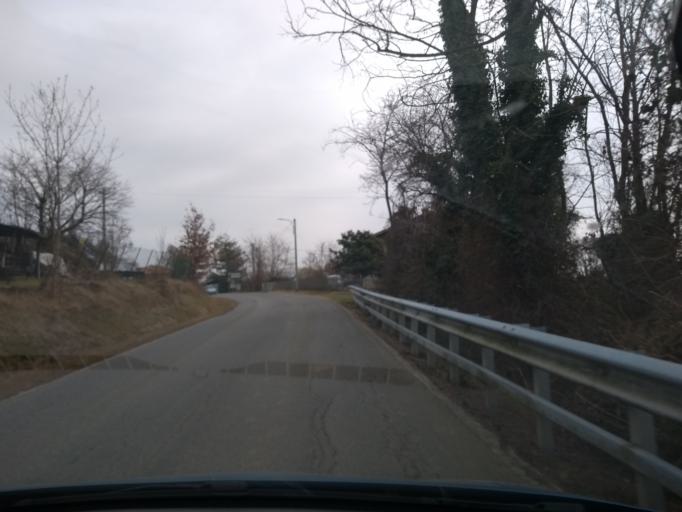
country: IT
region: Piedmont
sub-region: Provincia di Biella
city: Zubiena
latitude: 45.4912
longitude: 7.9913
